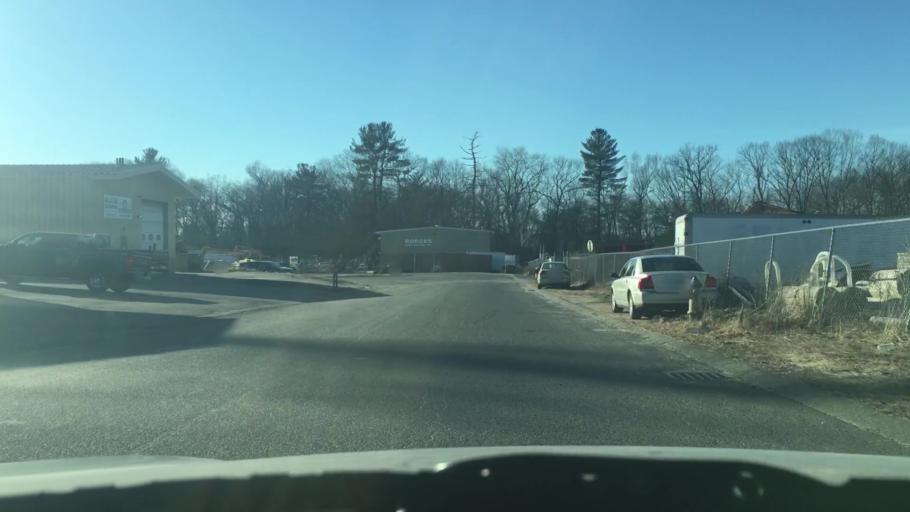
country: US
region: Massachusetts
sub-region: Hampden County
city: Ludlow
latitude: 42.1726
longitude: -72.4497
